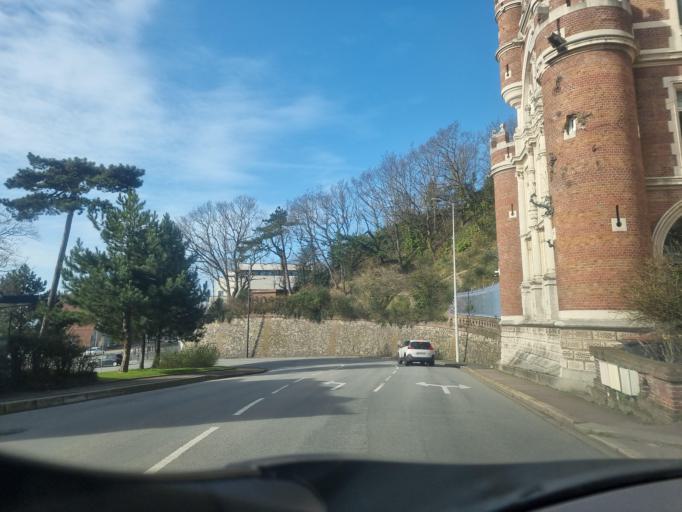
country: FR
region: Haute-Normandie
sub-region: Departement de la Seine-Maritime
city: Sainte-Adresse
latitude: 49.5010
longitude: 0.0921
